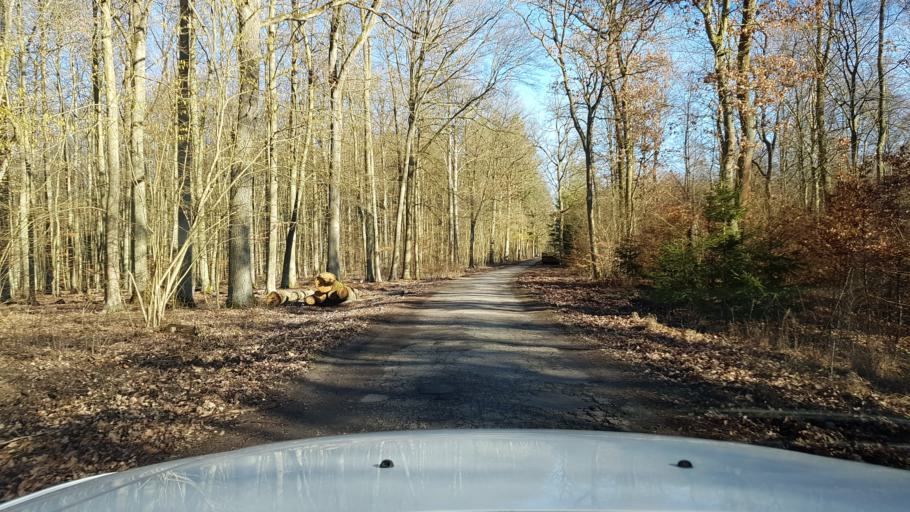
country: PL
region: West Pomeranian Voivodeship
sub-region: Powiat pyrzycki
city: Lipiany
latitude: 53.0317
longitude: 15.0251
